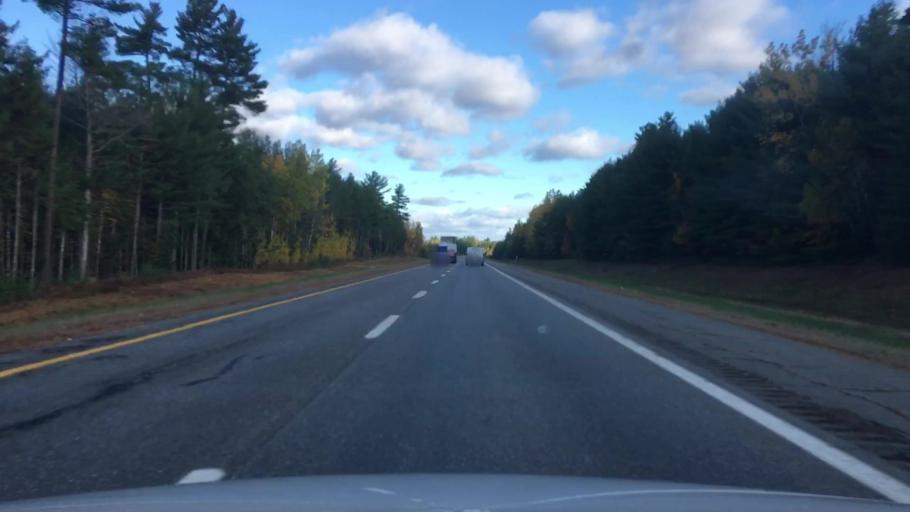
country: US
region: Maine
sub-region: Penobscot County
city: Greenbush
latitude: 45.1414
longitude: -68.7007
